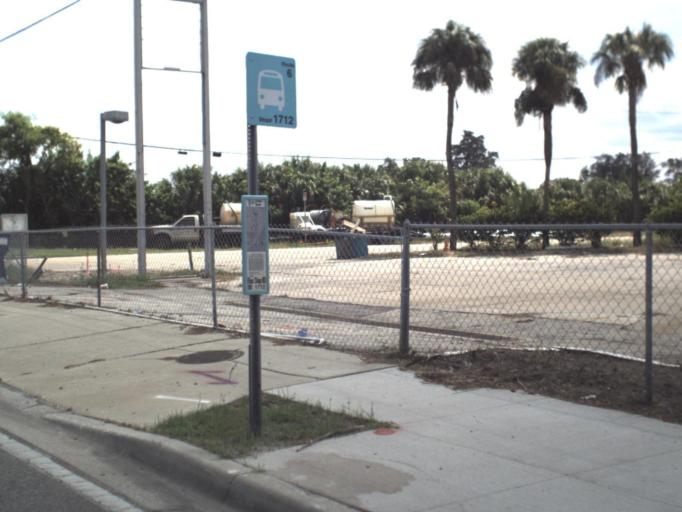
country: US
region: Florida
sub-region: Manatee County
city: Cortez
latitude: 27.4616
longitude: -82.6489
